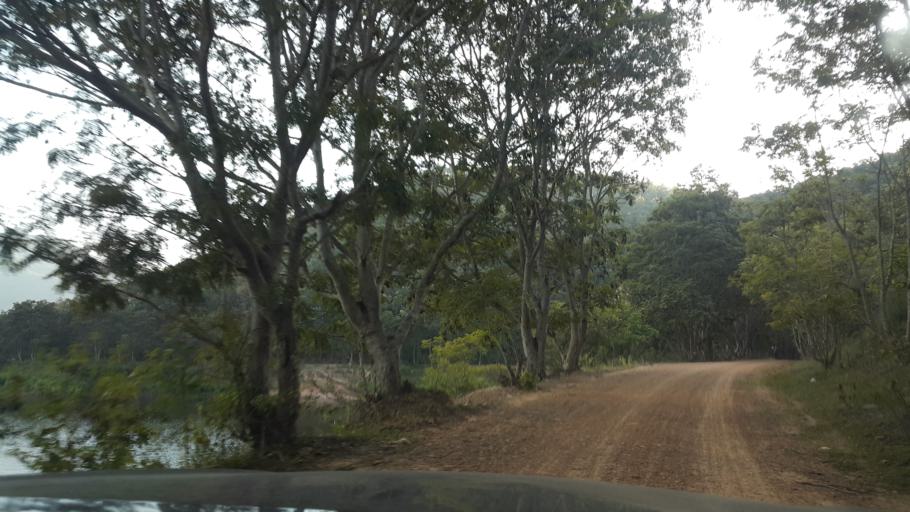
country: TH
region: Chiang Mai
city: Mae On
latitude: 18.7030
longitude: 99.2003
